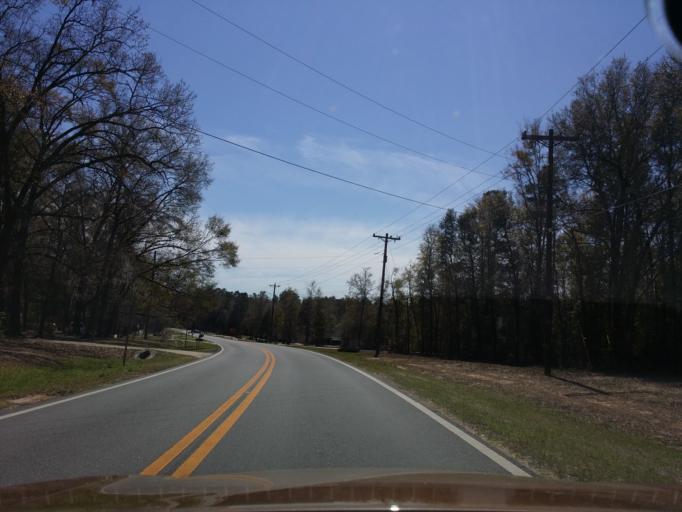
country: US
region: Florida
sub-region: Leon County
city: Woodville
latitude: 30.3745
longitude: -84.1259
